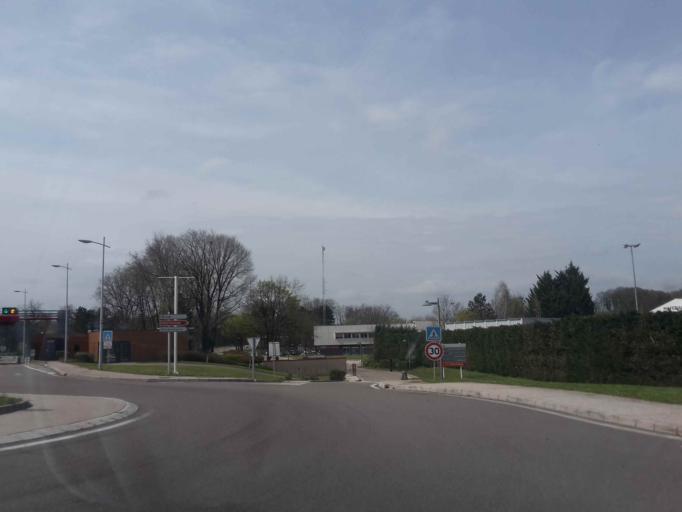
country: FR
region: Franche-Comte
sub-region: Departement du Doubs
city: Miserey-Salines
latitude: 47.2762
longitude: 5.9893
